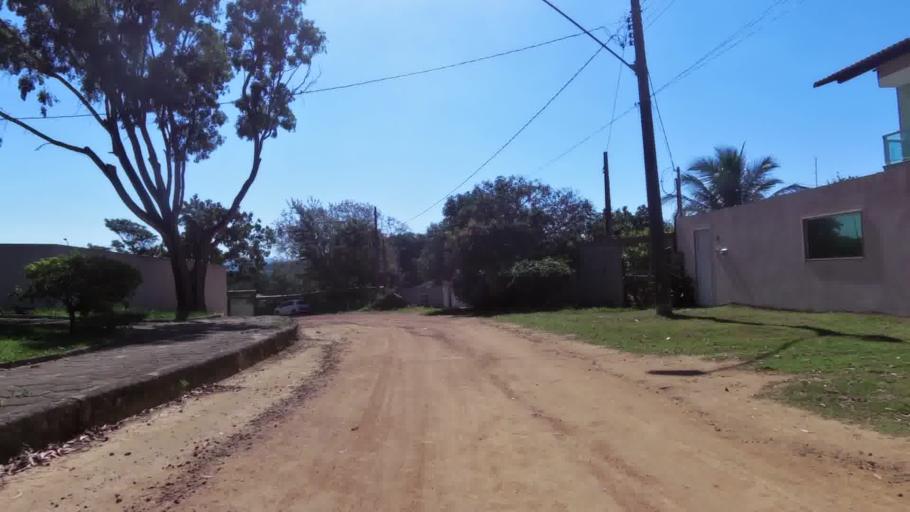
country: BR
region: Espirito Santo
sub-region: Guarapari
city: Guarapari
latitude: -20.7333
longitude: -40.5451
